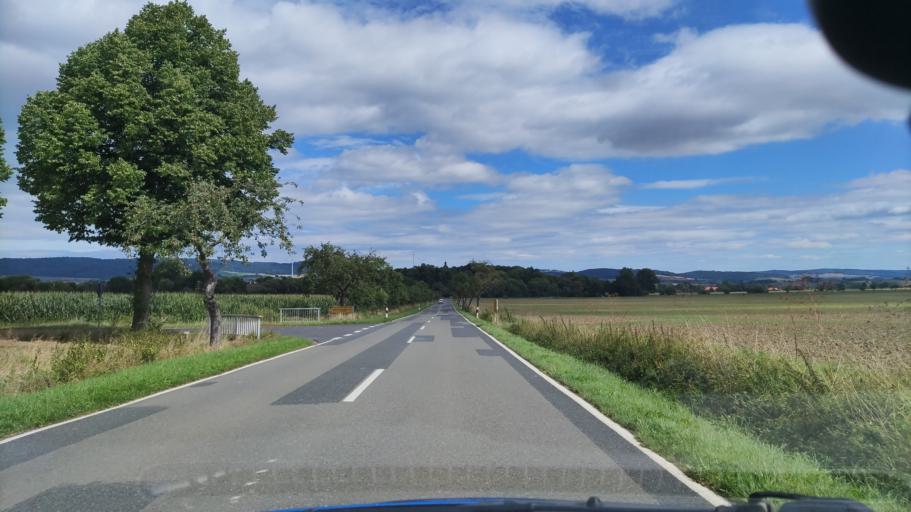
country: DE
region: Lower Saxony
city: Dassel
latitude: 51.8181
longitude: 9.7103
